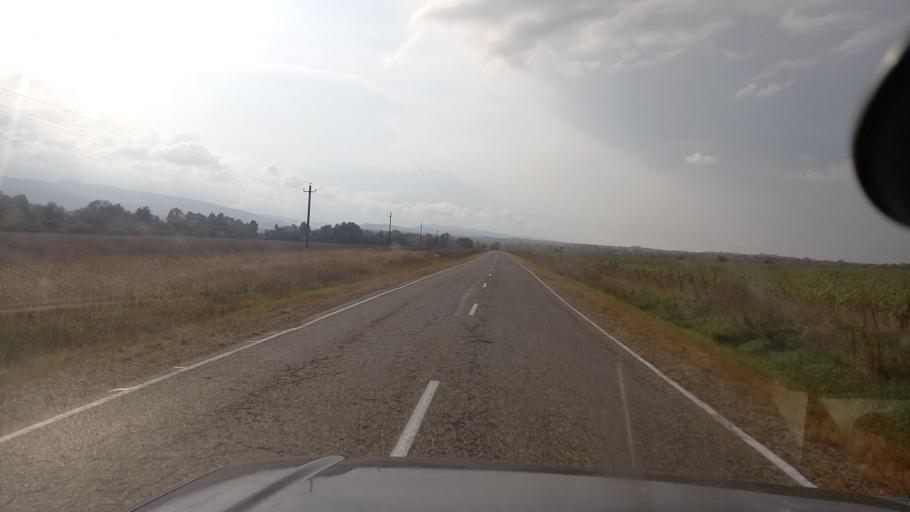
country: RU
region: Krasnodarskiy
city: Gubskaya
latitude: 44.3161
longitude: 40.5846
